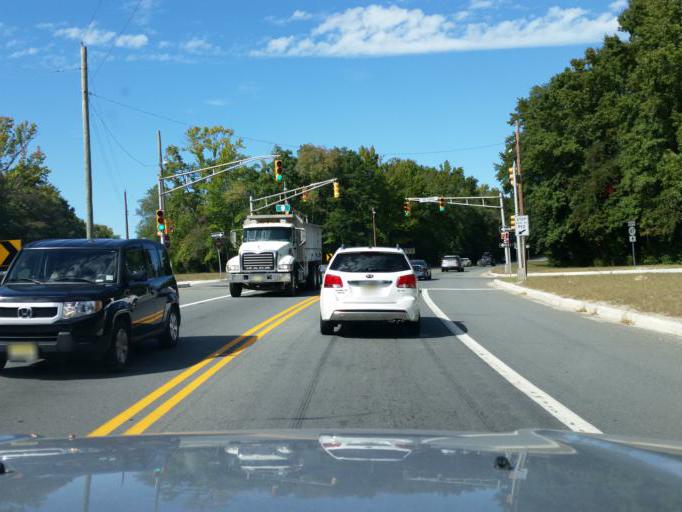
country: US
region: New Jersey
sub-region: Cumberland County
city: Laurel Lake
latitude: 39.3283
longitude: -74.9954
